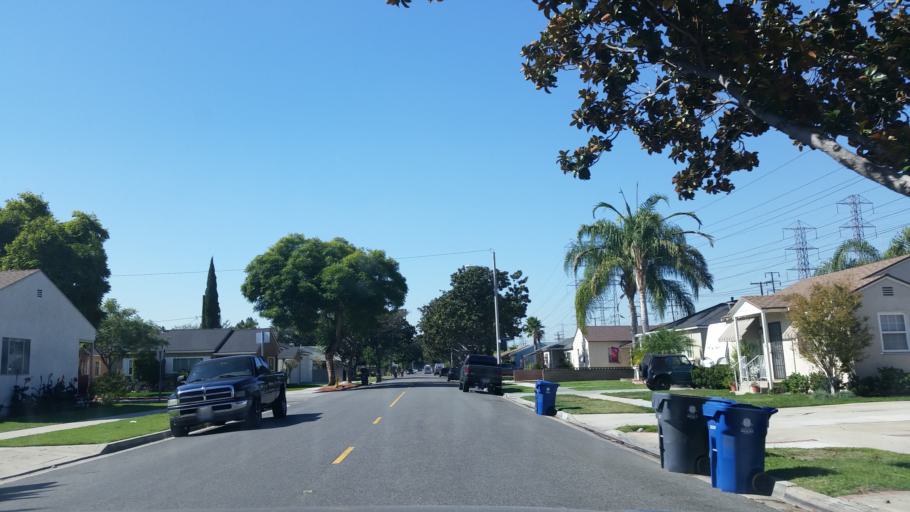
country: US
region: California
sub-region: Los Angeles County
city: Lakewood
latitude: 33.8679
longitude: -118.1294
